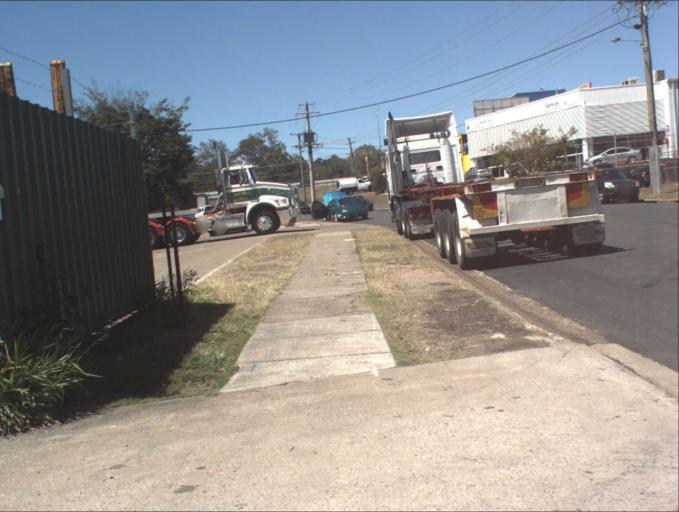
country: AU
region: Queensland
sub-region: Logan
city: Springwood
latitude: -27.6235
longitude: 153.1262
